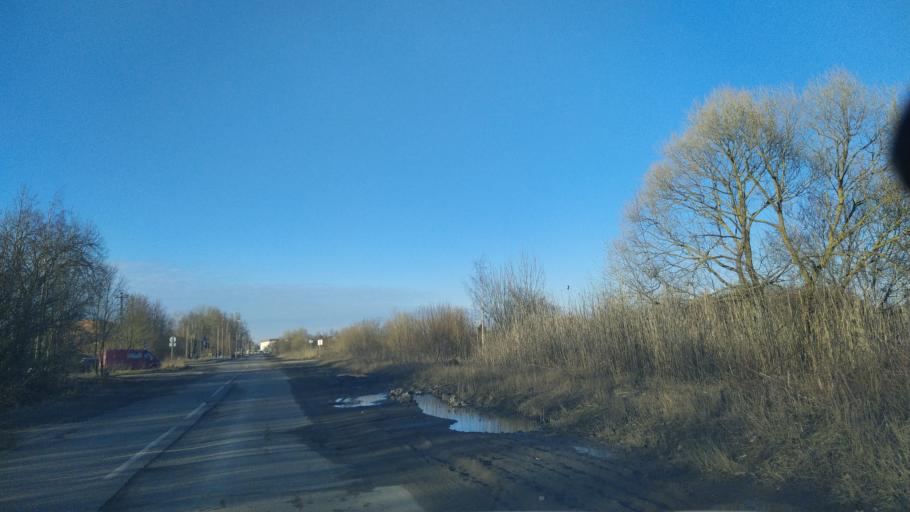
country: RU
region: St.-Petersburg
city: Pushkin
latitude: 59.6944
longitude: 30.3960
